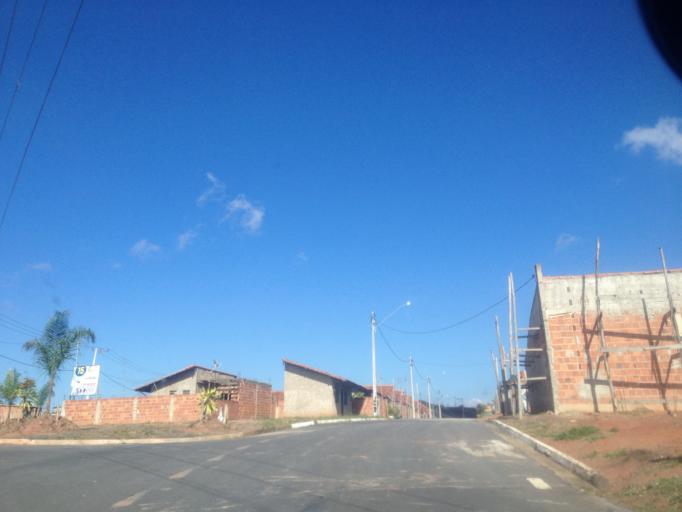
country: BR
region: Rio de Janeiro
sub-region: Porto Real
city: Porto Real
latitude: -22.4423
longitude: -44.3186
